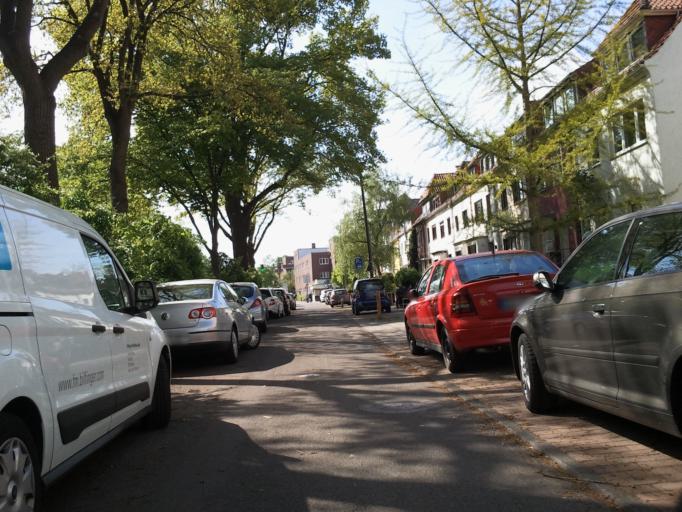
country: DE
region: Bremen
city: Bremen
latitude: 53.0766
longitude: 8.8392
